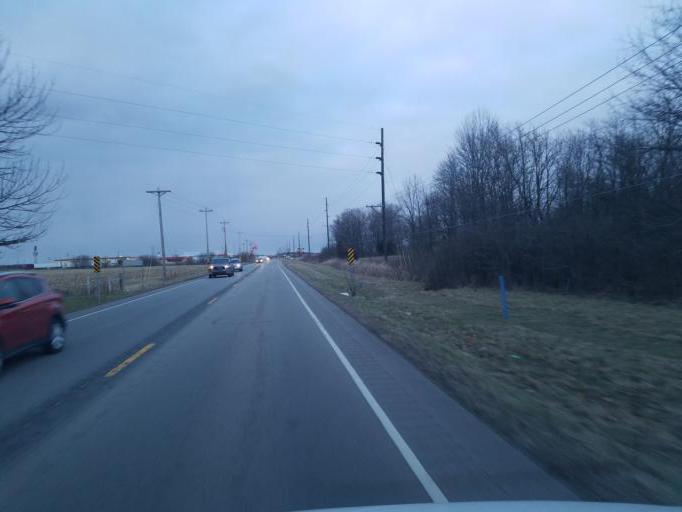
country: US
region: Indiana
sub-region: Henry County
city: New Castle
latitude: 39.8452
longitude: -85.4224
